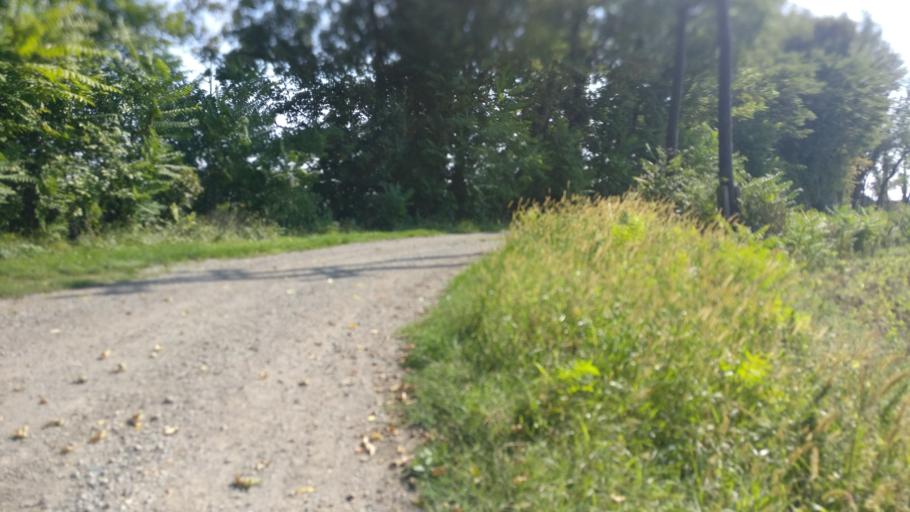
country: AT
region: Lower Austria
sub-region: Politischer Bezirk Baden
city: Ebreichsdorf
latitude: 47.9871
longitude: 16.4102
